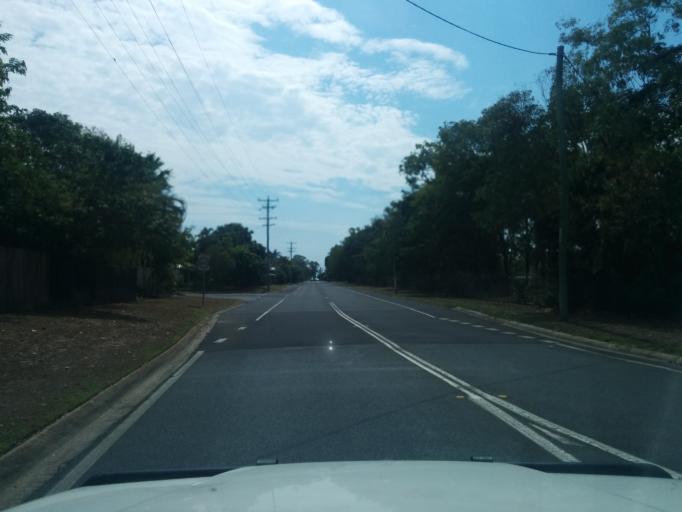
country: AU
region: Queensland
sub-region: Cairns
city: Yorkeys Knob
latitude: -16.8419
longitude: 145.7357
